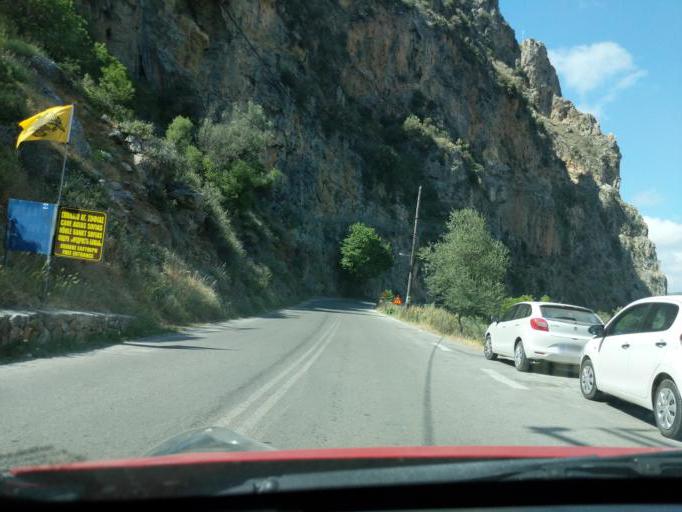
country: GR
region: Crete
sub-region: Nomos Chanias
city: Kissamos
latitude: 35.4113
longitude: 23.6824
